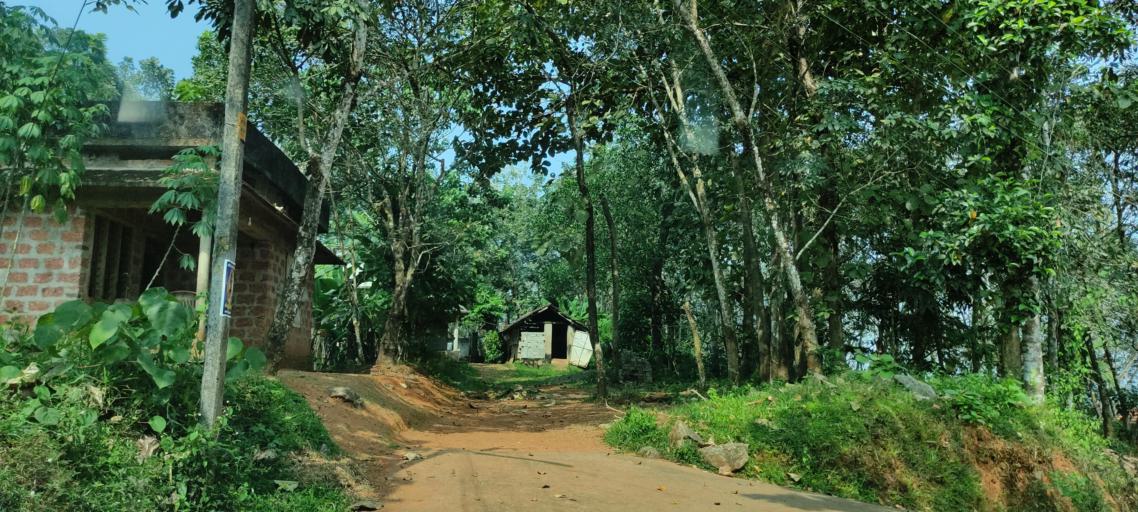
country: IN
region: Kerala
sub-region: Pattanamtitta
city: Adur
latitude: 9.2140
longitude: 76.6932
